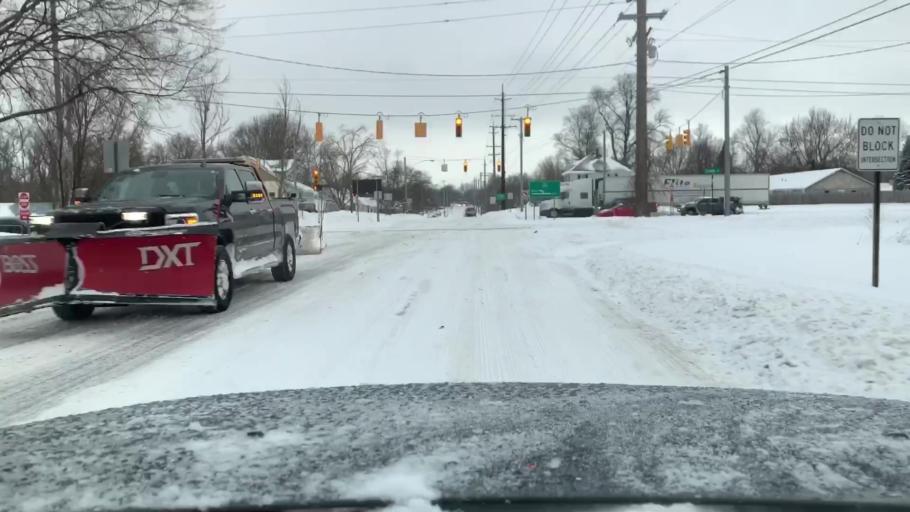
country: US
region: Michigan
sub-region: Ottawa County
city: Zeeland
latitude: 42.8049
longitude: -86.0384
